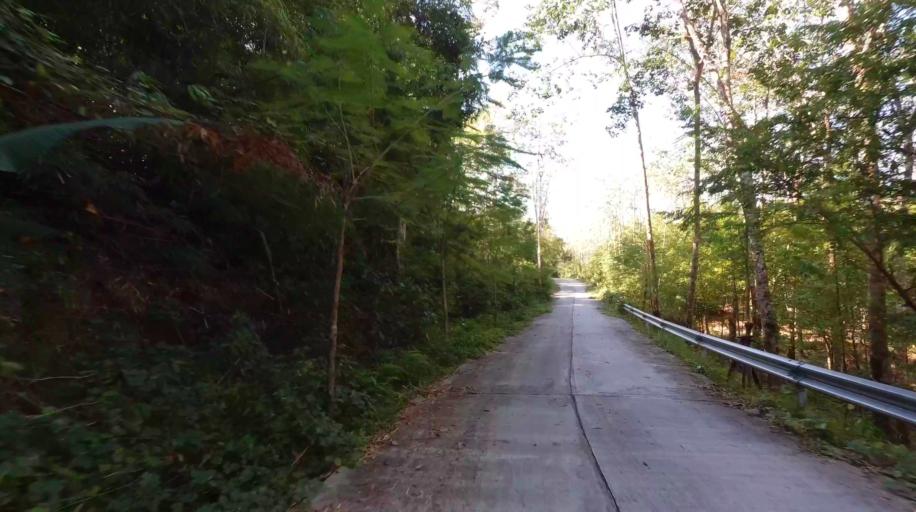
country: TH
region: Trat
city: Ko Kut
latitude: 11.6265
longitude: 102.5564
